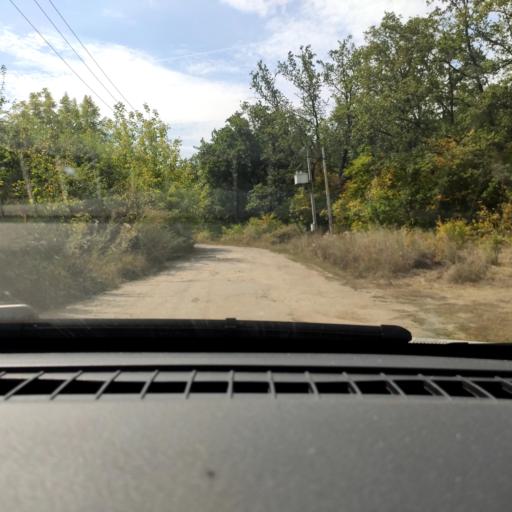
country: RU
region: Voronezj
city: Pridonskoy
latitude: 51.7511
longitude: 39.0767
